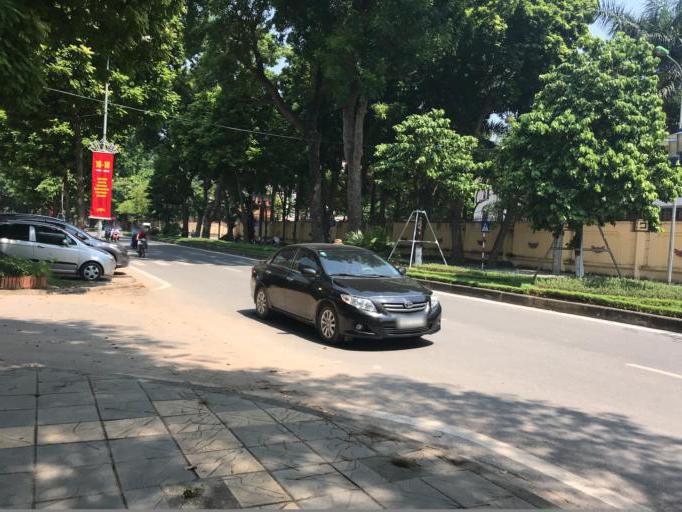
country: VN
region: Ha Noi
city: Hanoi
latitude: 21.0364
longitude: 105.8411
